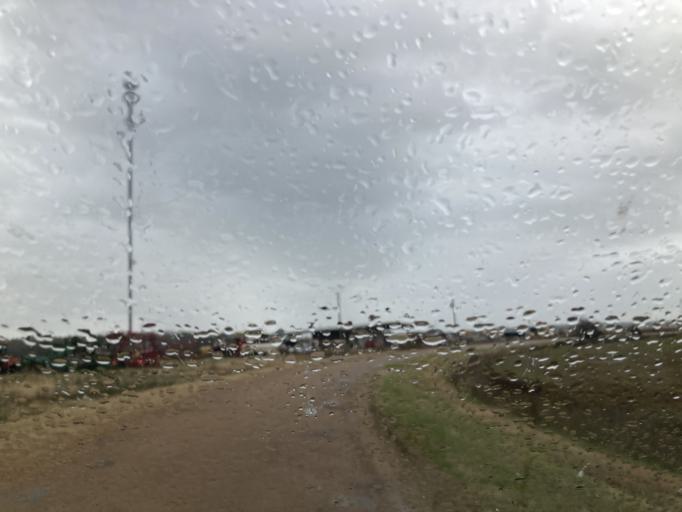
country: US
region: Mississippi
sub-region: Yazoo County
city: Yazoo City
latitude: 32.9874
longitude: -90.4478
